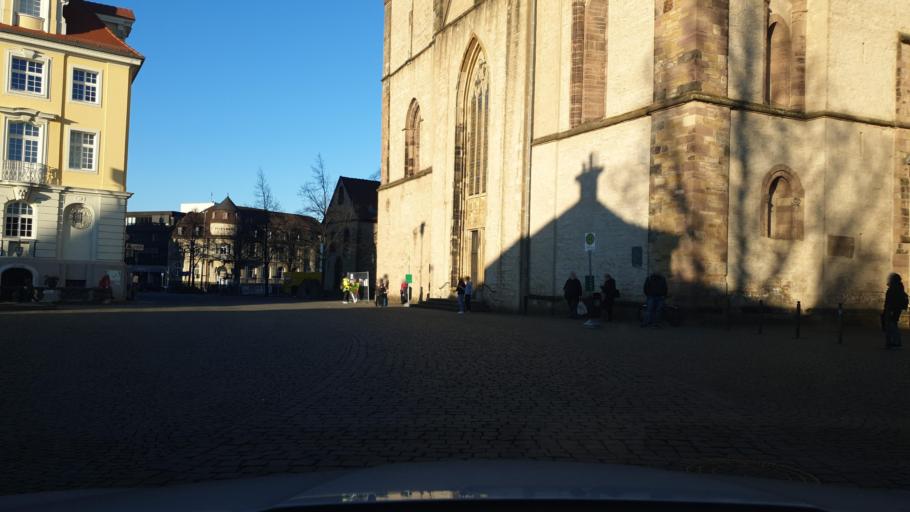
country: DE
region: North Rhine-Westphalia
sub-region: Regierungsbezirk Detmold
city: Herford
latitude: 52.1154
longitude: 8.6705
